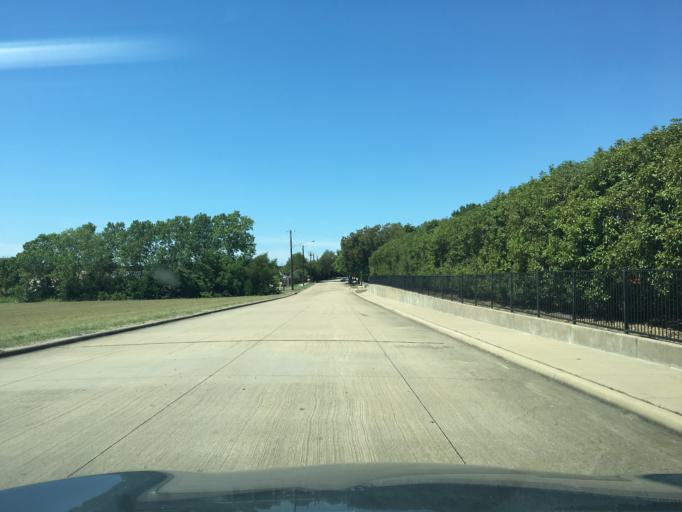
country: US
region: Texas
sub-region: Dallas County
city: Sachse
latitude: 32.9605
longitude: -96.6314
